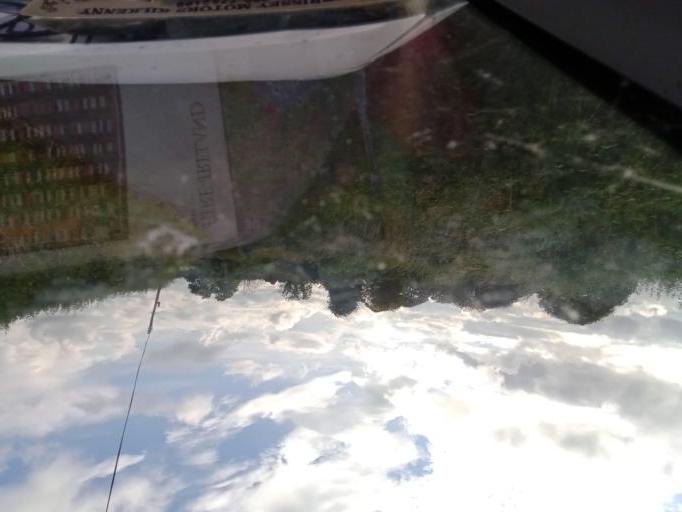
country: IE
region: Leinster
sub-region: Laois
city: Rathdowney
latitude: 52.7879
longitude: -7.5537
